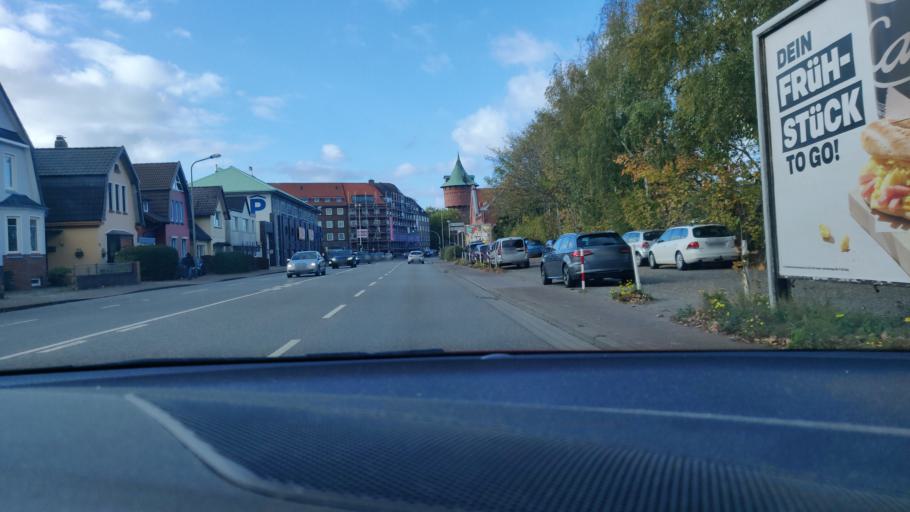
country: DE
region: Lower Saxony
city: Cuxhaven
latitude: 53.8600
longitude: 8.7045
